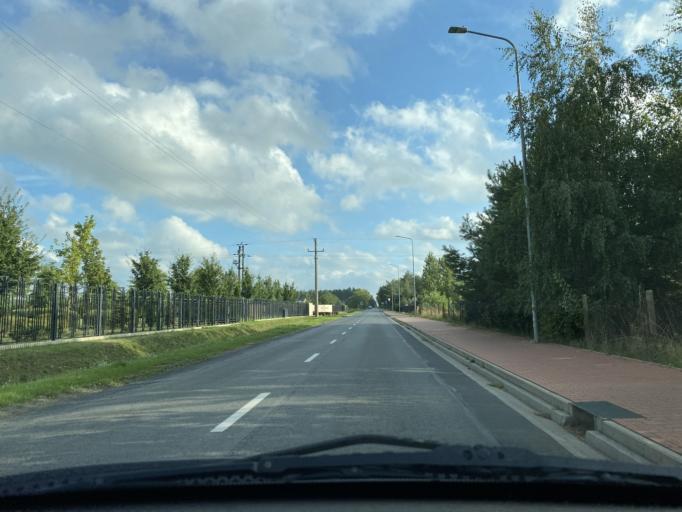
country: PL
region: Greater Poland Voivodeship
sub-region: Powiat poznanski
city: Baranowo
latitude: 52.4166
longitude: 16.7182
